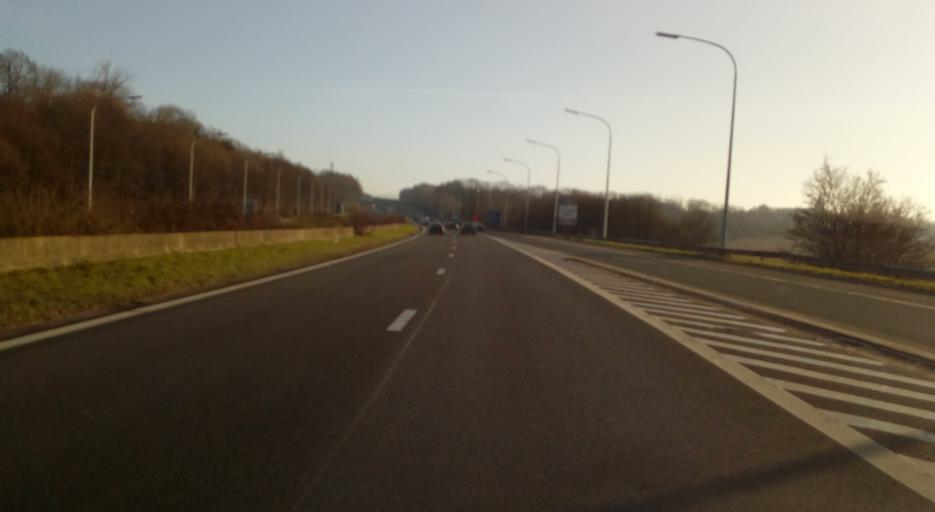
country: BE
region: Wallonia
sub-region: Province du Hainaut
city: Courcelles
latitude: 50.4601
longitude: 4.4198
